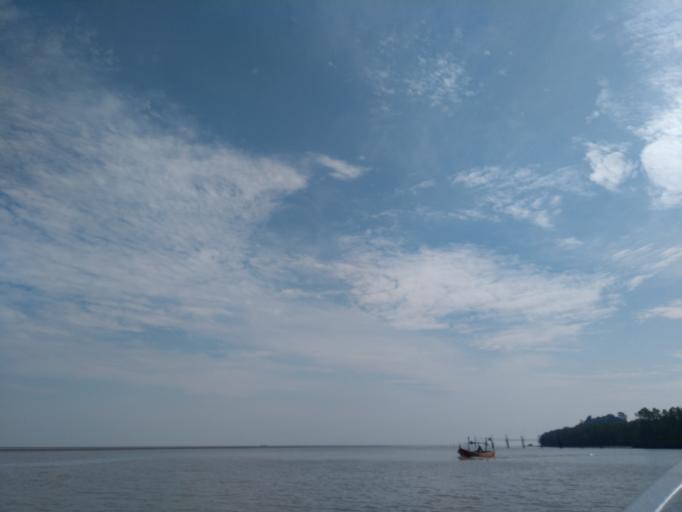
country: MY
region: Sarawak
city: Kuching
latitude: 1.6839
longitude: 110.4262
